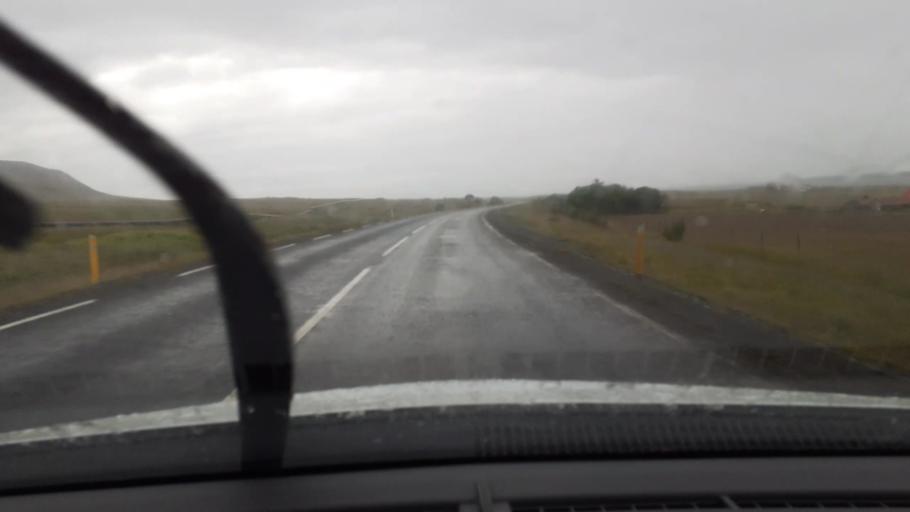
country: IS
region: West
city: Borgarnes
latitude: 64.3655
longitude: -21.9010
